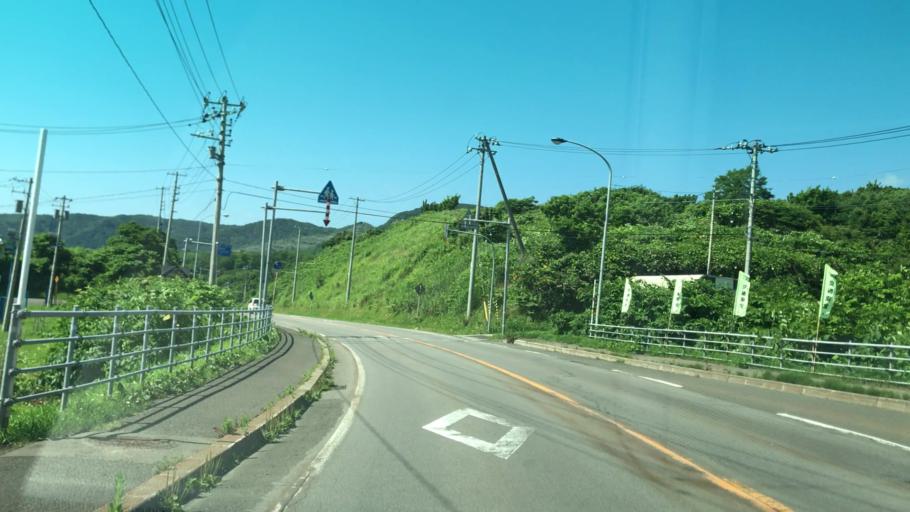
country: JP
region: Hokkaido
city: Iwanai
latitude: 43.0640
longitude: 140.4984
